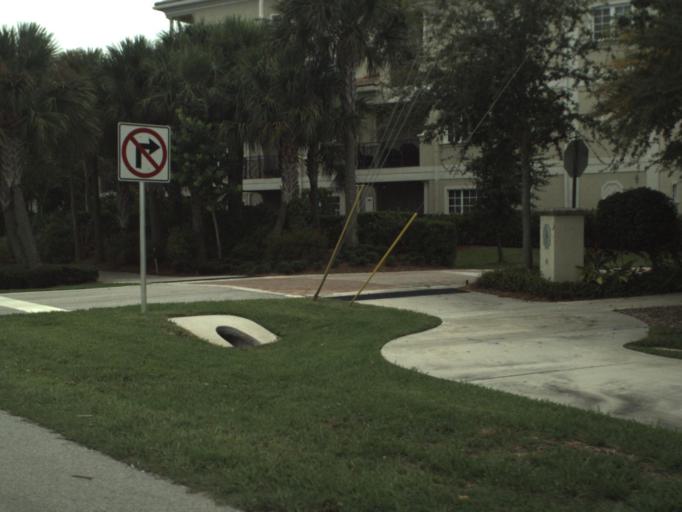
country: US
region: Florida
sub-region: Palm Beach County
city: Jupiter
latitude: 26.9208
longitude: -80.0742
